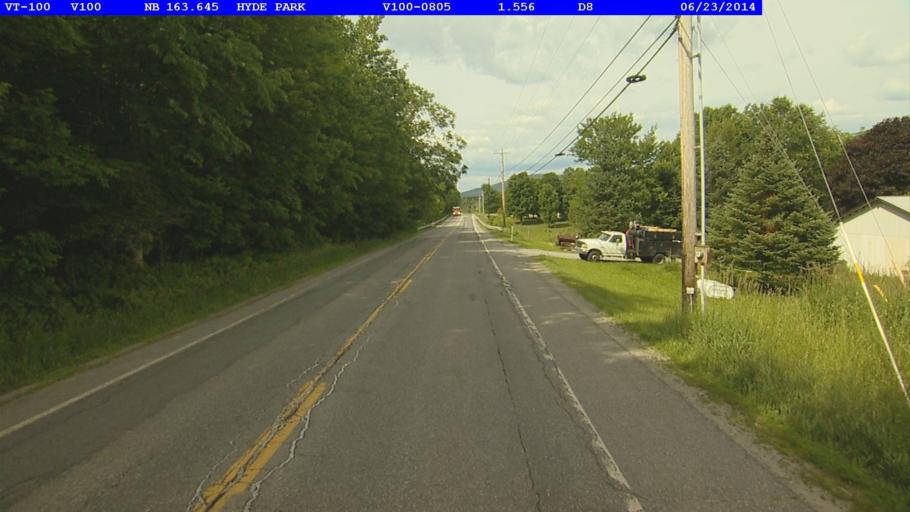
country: US
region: Vermont
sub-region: Lamoille County
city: Hyde Park
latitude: 44.6179
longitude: -72.6038
